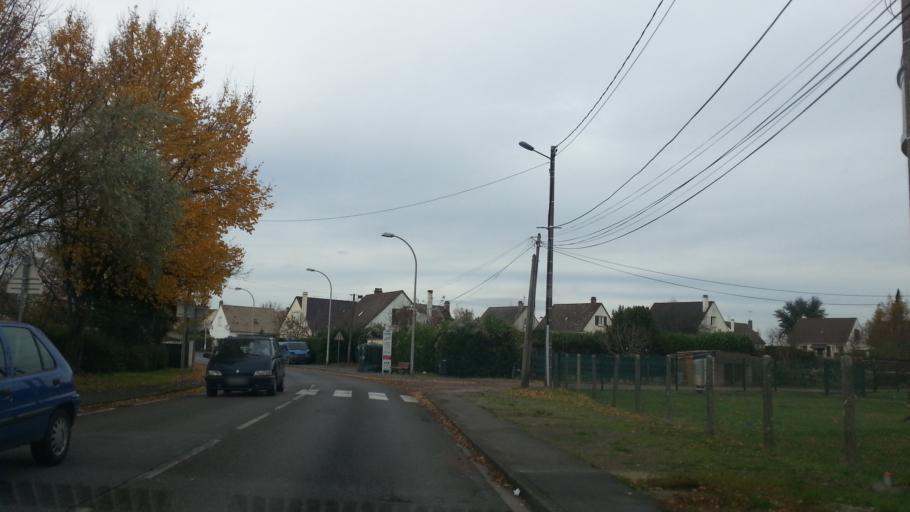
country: FR
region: Picardie
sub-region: Departement de l'Oise
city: Montataire
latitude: 49.2582
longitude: 2.4411
